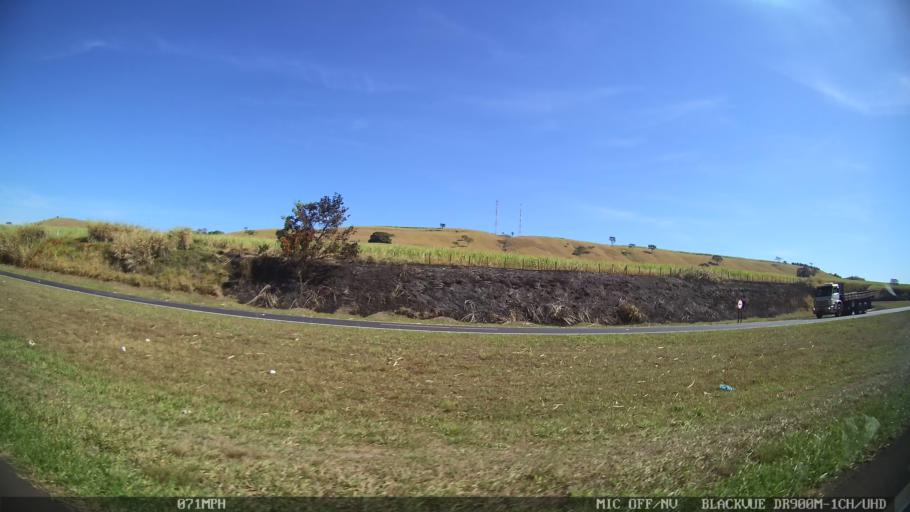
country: BR
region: Sao Paulo
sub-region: Sao Simao
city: Sao Simao
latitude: -21.4701
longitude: -47.6406
